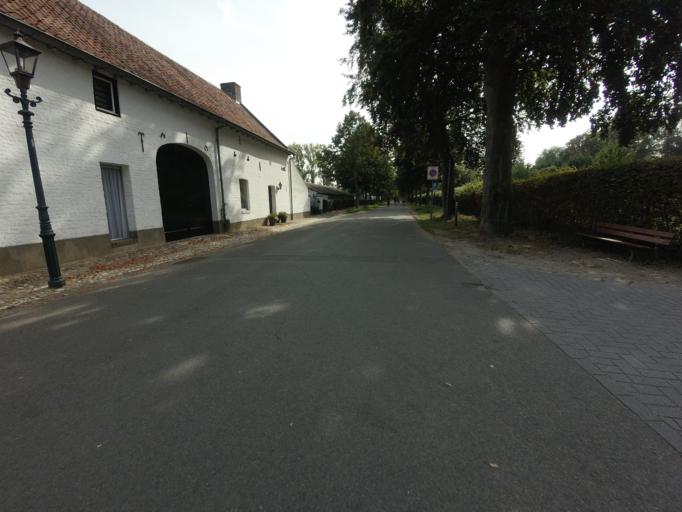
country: NL
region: Limburg
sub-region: Gemeente Maasgouw
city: Maasbracht
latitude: 51.1597
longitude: 5.8429
